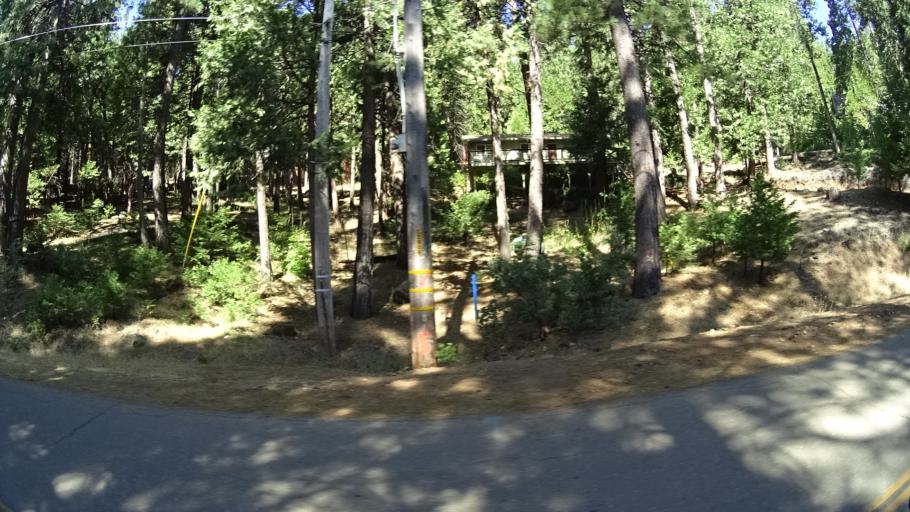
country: US
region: California
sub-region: Calaveras County
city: Arnold
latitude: 38.2498
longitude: -120.3677
